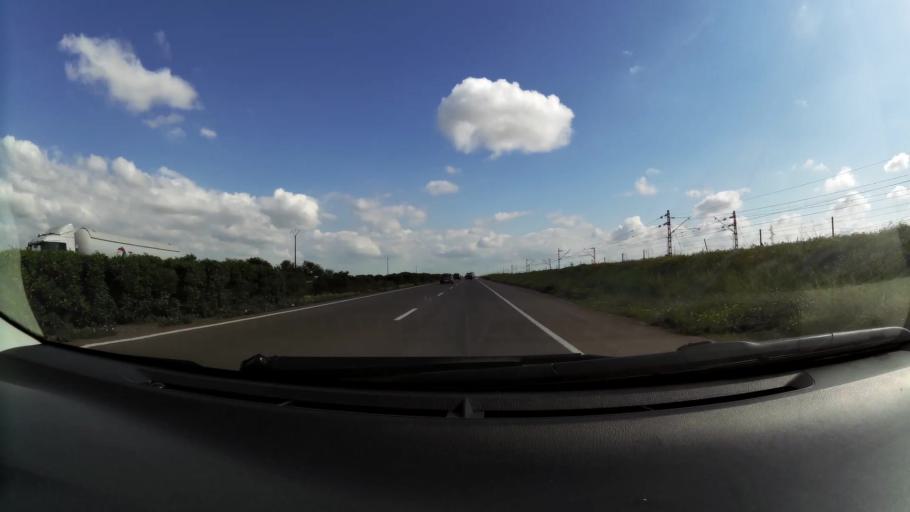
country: MA
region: Chaouia-Ouardigha
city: Nouaseur
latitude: 33.3545
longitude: -7.6174
